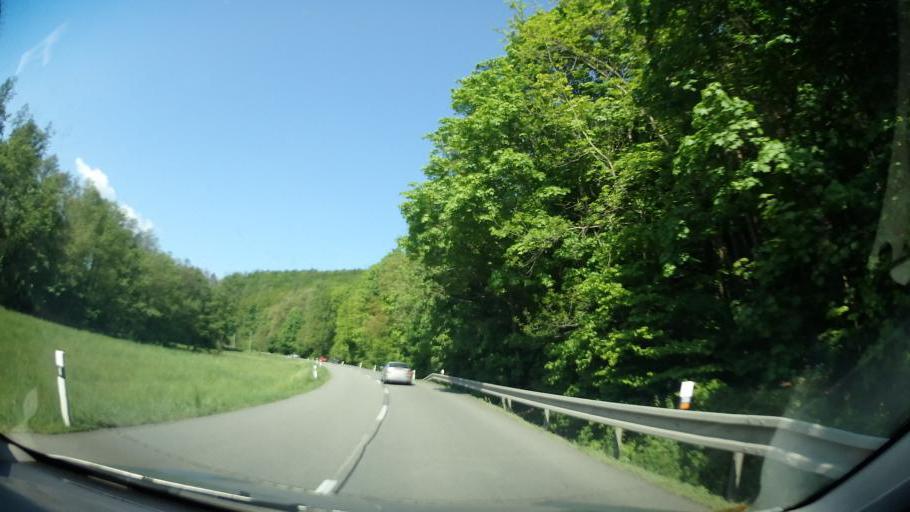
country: CZ
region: South Moravian
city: Zastavka
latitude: 49.1903
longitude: 16.3474
